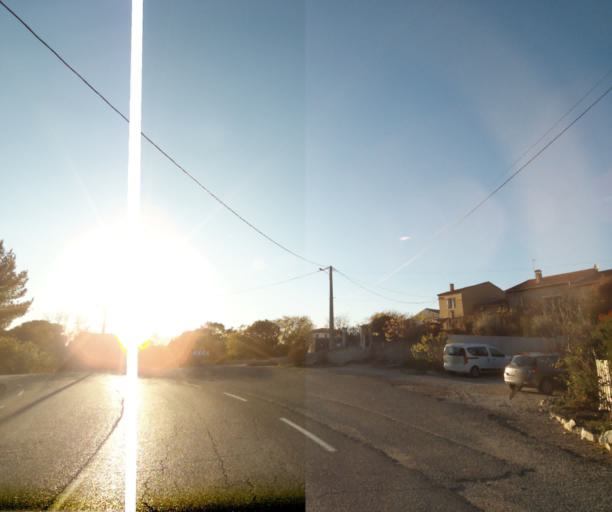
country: FR
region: Provence-Alpes-Cote d'Azur
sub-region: Departement des Bouches-du-Rhone
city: Carnoux-en-Provence
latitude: 43.2445
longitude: 5.5668
